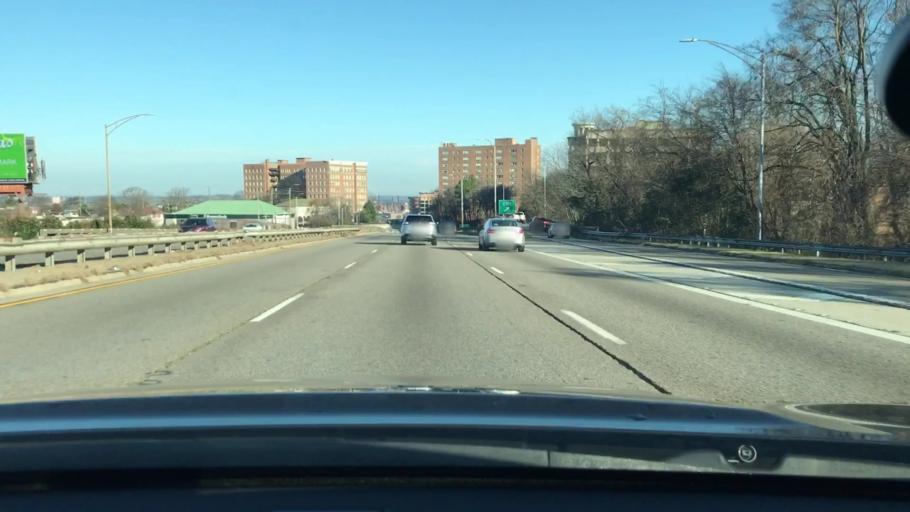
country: US
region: Alabama
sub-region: Jefferson County
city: Birmingham
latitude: 33.4991
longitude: -86.7891
